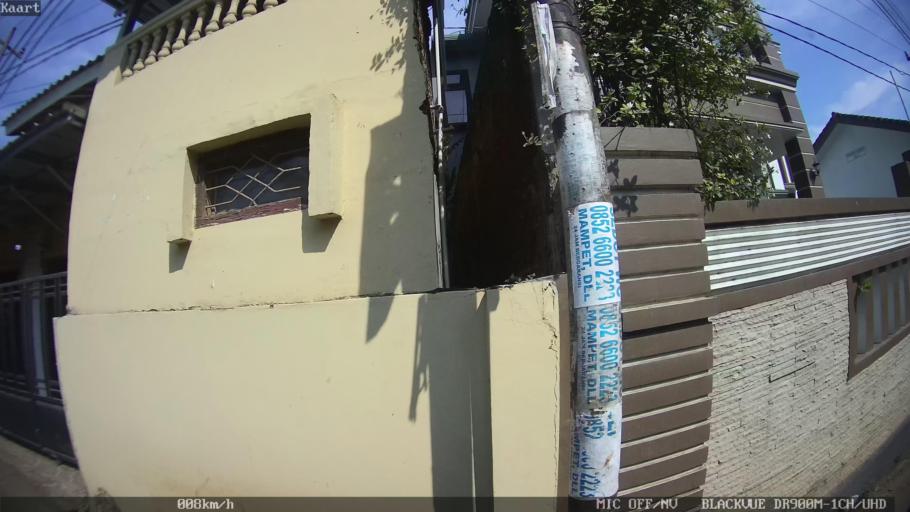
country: ID
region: Lampung
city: Kedaton
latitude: -5.3727
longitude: 105.2390
